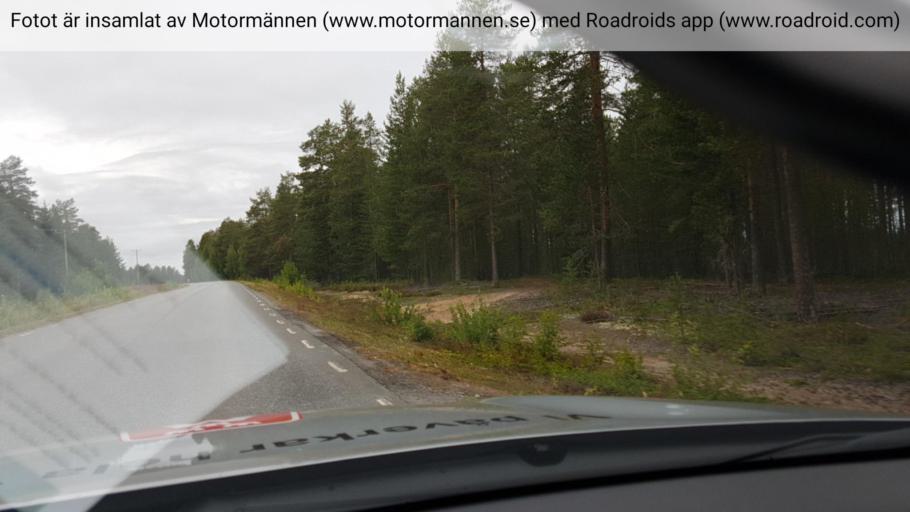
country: SE
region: Norrbotten
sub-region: Bodens Kommun
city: Boden
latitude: 65.8150
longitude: 21.5968
